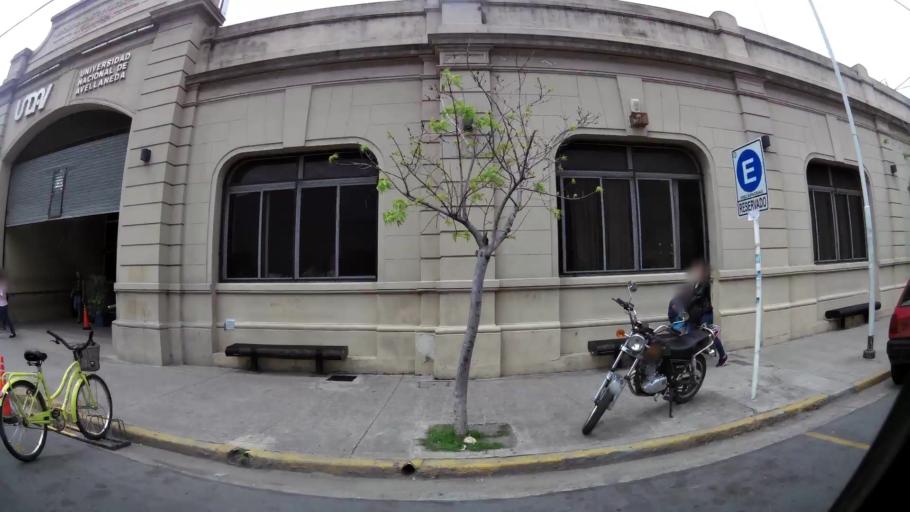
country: AR
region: Buenos Aires
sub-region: Partido de Avellaneda
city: Avellaneda
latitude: -34.6630
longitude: -58.3724
